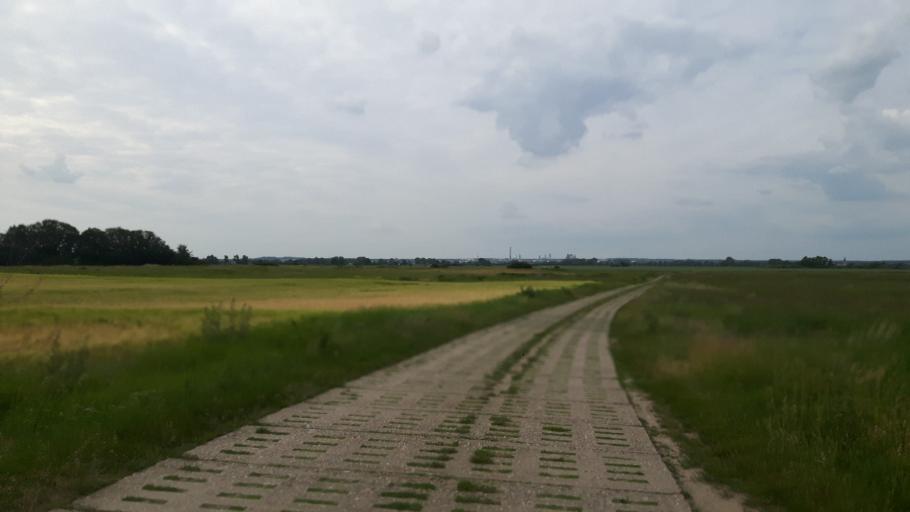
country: DE
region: Saxony-Anhalt
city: Bergwitz
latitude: 51.8303
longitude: 12.6085
